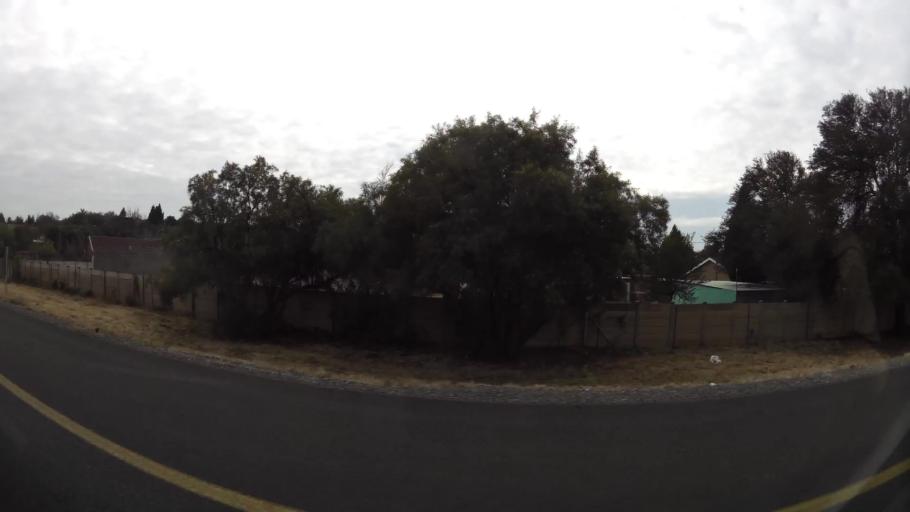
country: ZA
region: Orange Free State
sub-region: Mangaung Metropolitan Municipality
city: Bloemfontein
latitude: -29.1590
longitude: 26.1780
